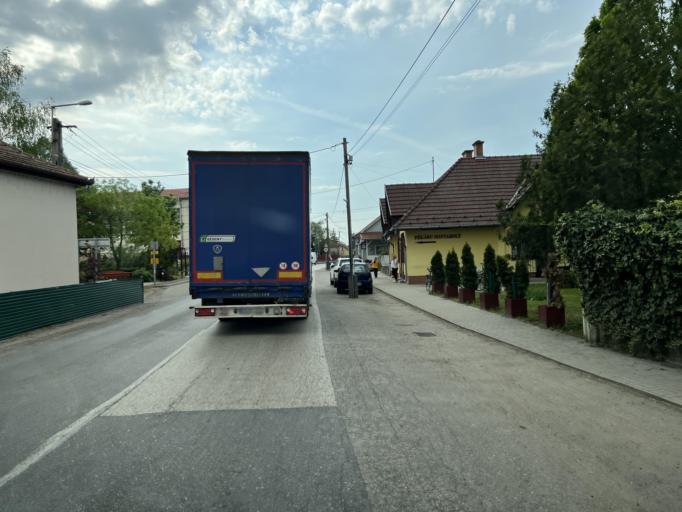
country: HU
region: Pest
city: Farmos
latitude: 47.3616
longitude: 19.8467
